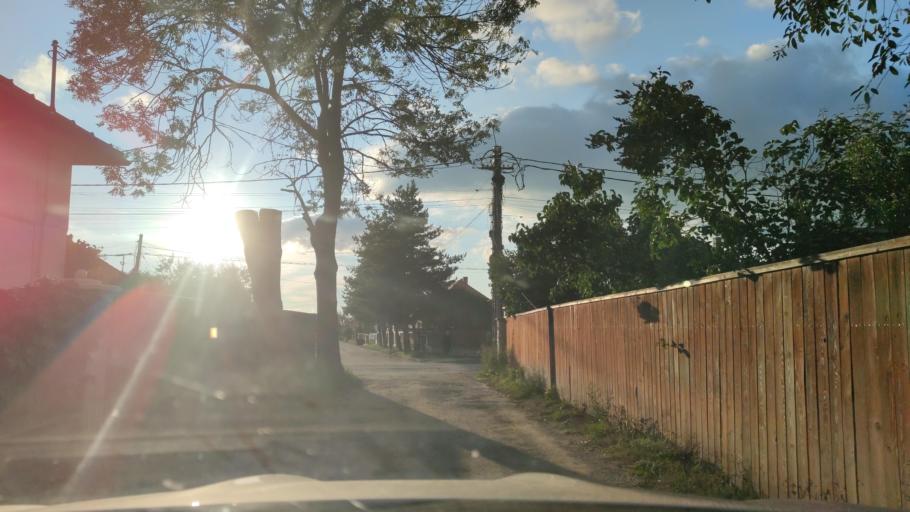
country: RO
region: Harghita
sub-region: Municipiul Gheorgheni
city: Gheorgheni
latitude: 46.7253
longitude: 25.6021
